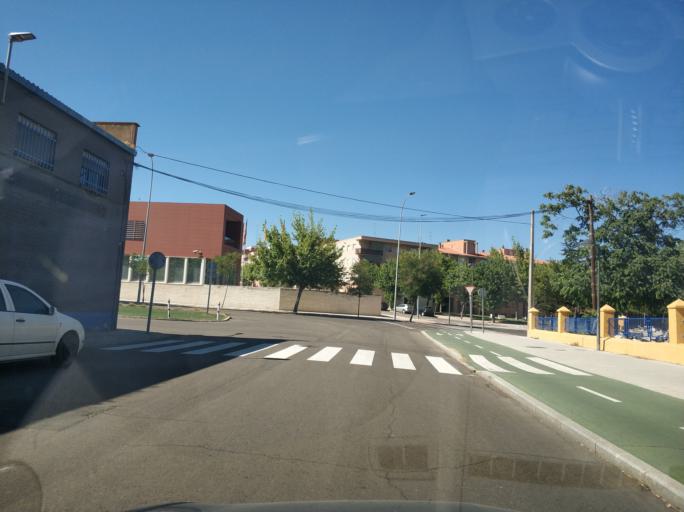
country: ES
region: Castille and Leon
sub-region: Provincia de Salamanca
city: Salamanca
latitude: 40.9587
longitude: -5.6494
